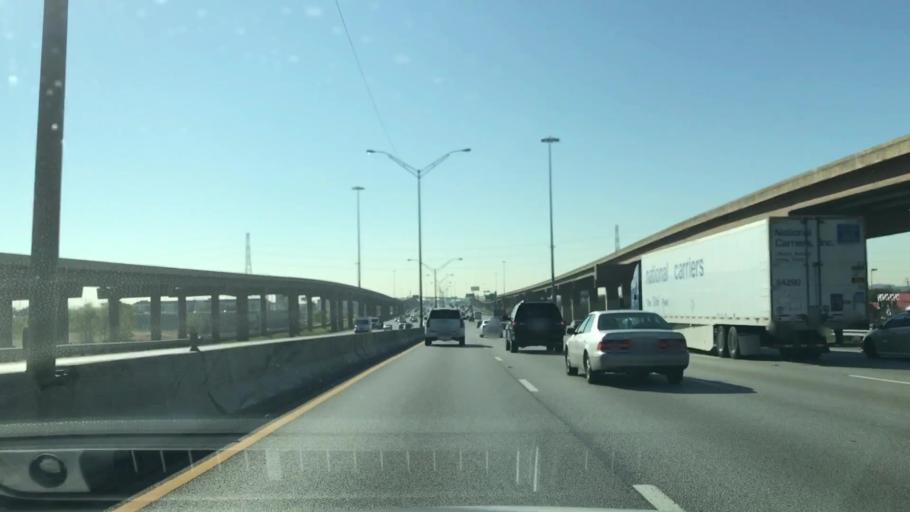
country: US
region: Texas
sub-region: Dallas County
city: Farmers Branch
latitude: 32.8870
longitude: -96.8982
